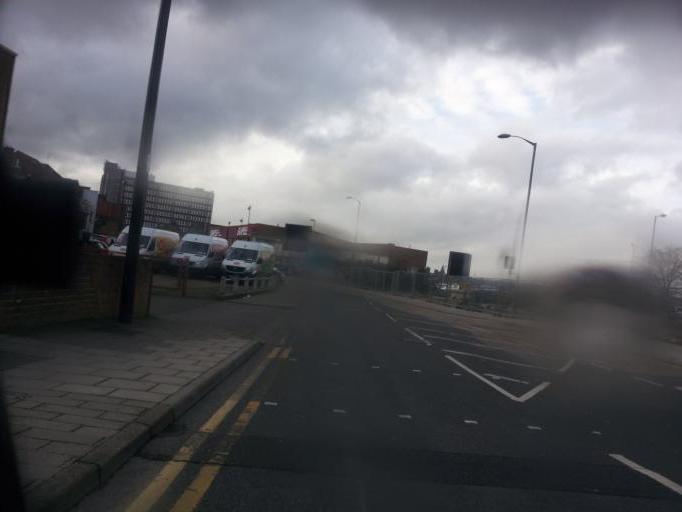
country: GB
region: England
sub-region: Kent
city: Chatham
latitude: 51.3842
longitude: 0.5237
